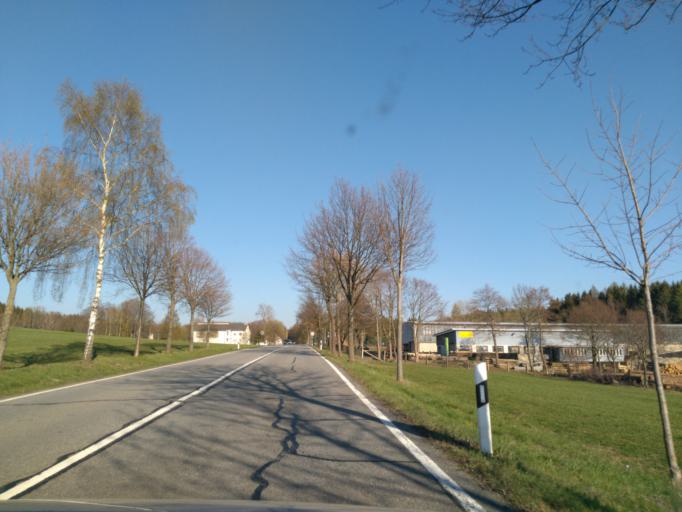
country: DE
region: Saxony
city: Schlettau
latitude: 50.5542
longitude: 12.9775
